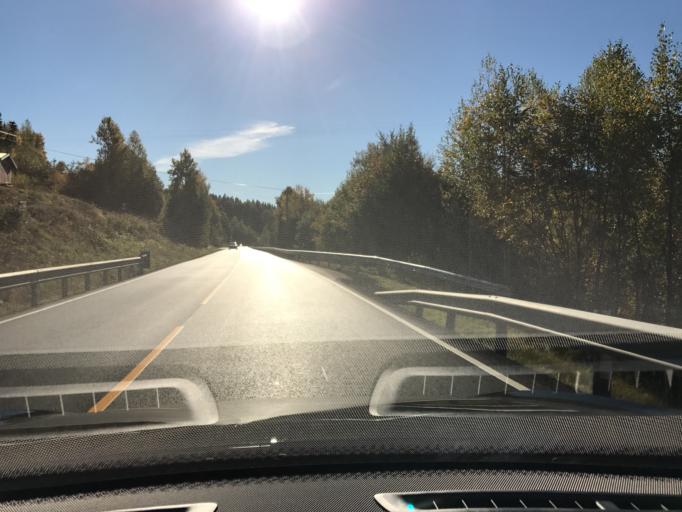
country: NO
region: Buskerud
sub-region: Krodsherad
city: Noresund
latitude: 60.3554
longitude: 9.6453
